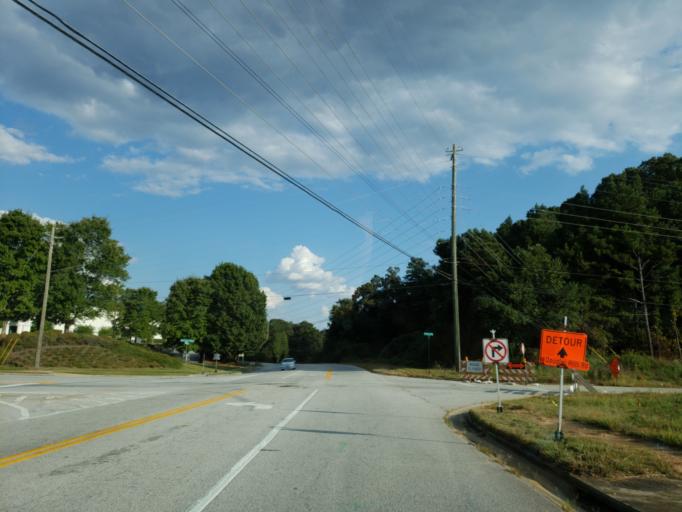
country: US
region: Georgia
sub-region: Cobb County
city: Mableton
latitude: 33.7557
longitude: -84.5855
